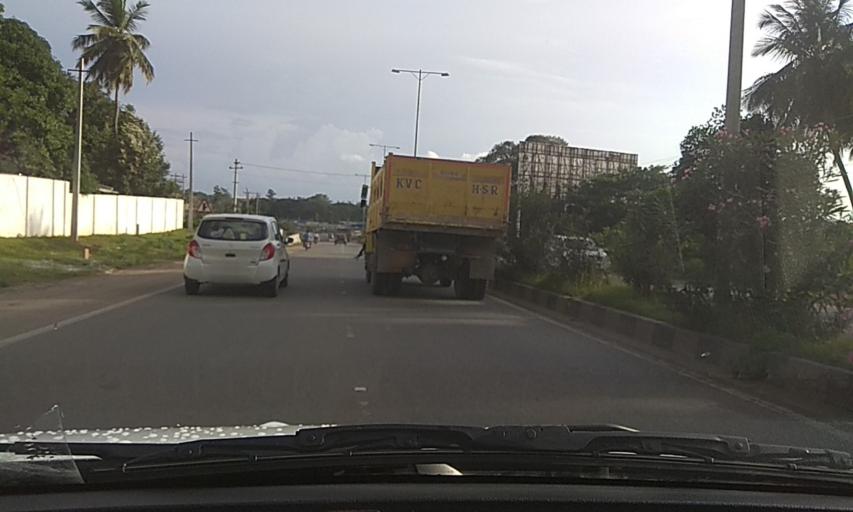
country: IN
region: Karnataka
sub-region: Mysore
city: Nanjangud
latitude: 12.1571
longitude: 76.6818
